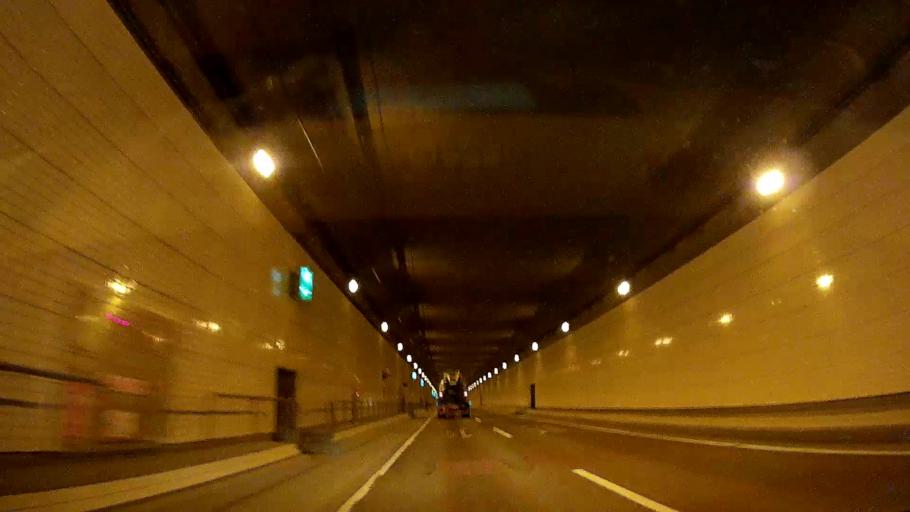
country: JP
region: Kanagawa
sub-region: Kawasaki-shi
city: Kawasaki
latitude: 35.5873
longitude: 139.7884
